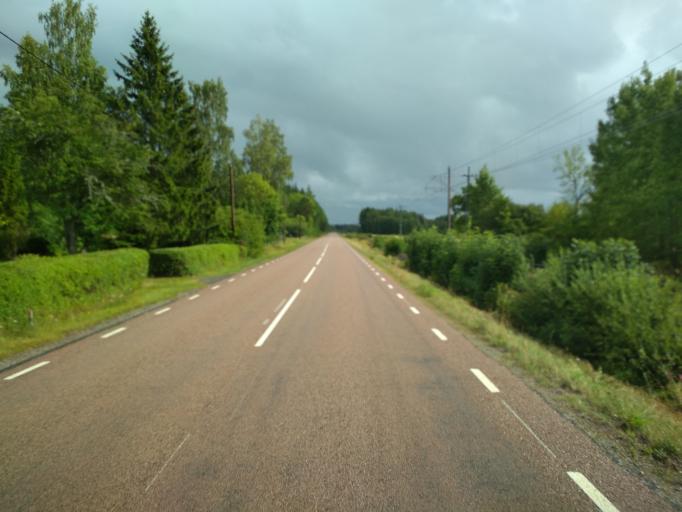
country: SE
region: Vaestmanland
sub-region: Surahammars Kommun
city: Ramnas
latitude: 59.8225
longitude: 16.1487
